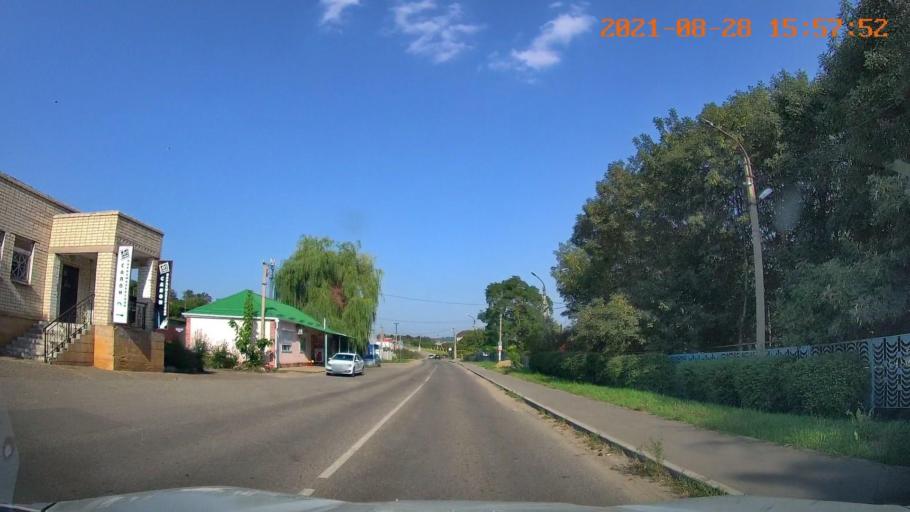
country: RU
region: Stavropol'skiy
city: Tatarka
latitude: 44.9611
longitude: 41.9454
